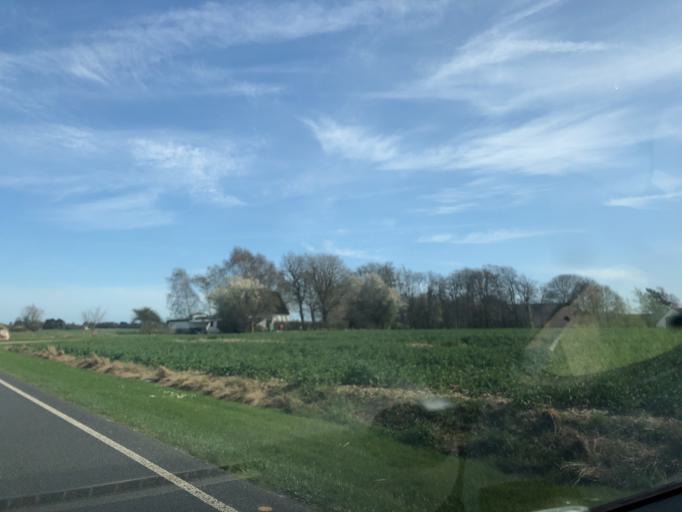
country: DK
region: Zealand
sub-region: Stevns Kommune
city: Harlev
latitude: 55.2779
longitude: 12.2411
